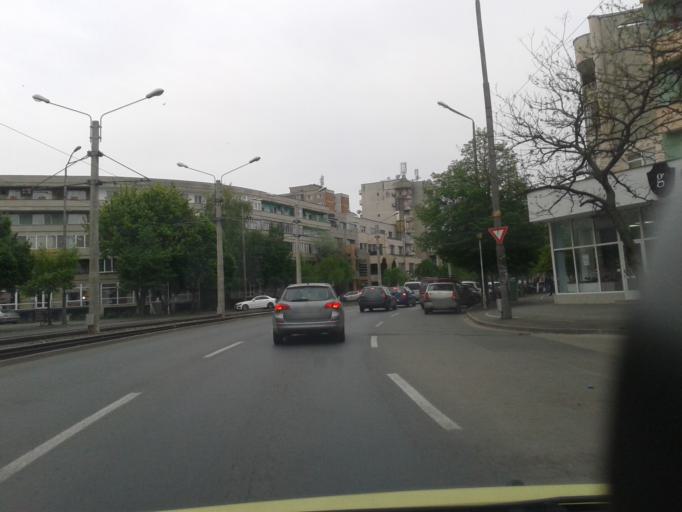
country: RO
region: Arad
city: Arad
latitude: 46.1882
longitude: 21.3251
